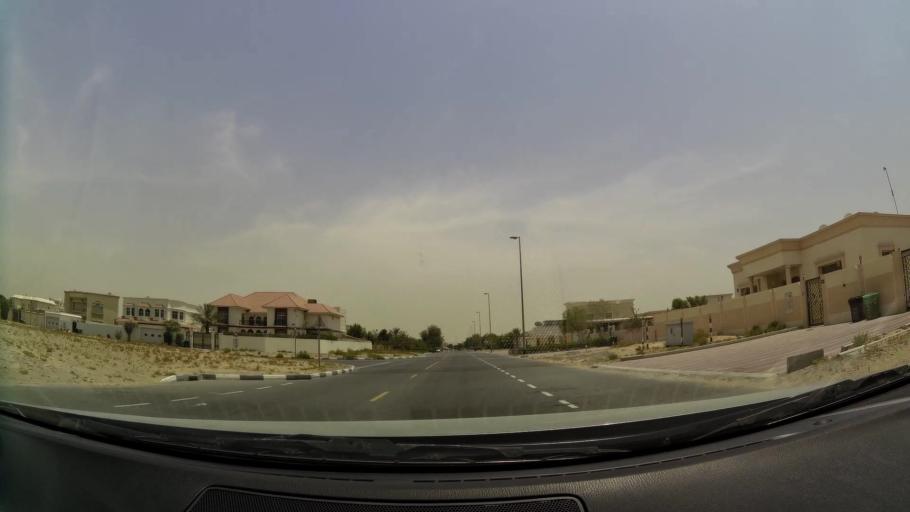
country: AE
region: Ash Shariqah
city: Sharjah
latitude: 25.1939
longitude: 55.3800
